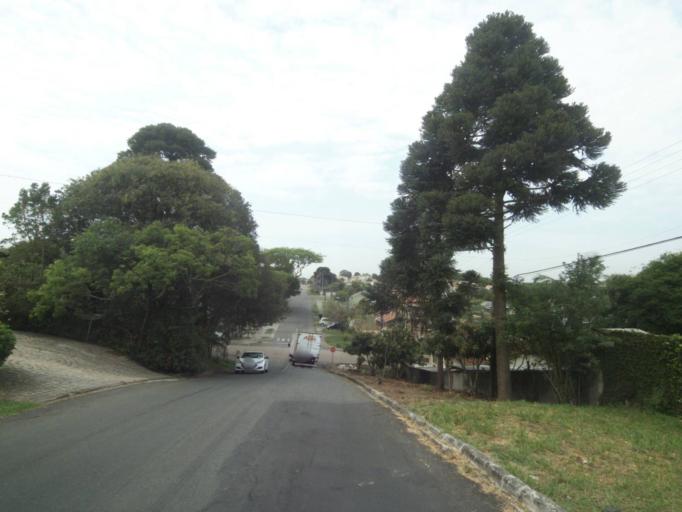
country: BR
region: Parana
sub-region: Pinhais
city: Pinhais
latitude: -25.4166
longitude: -49.2122
